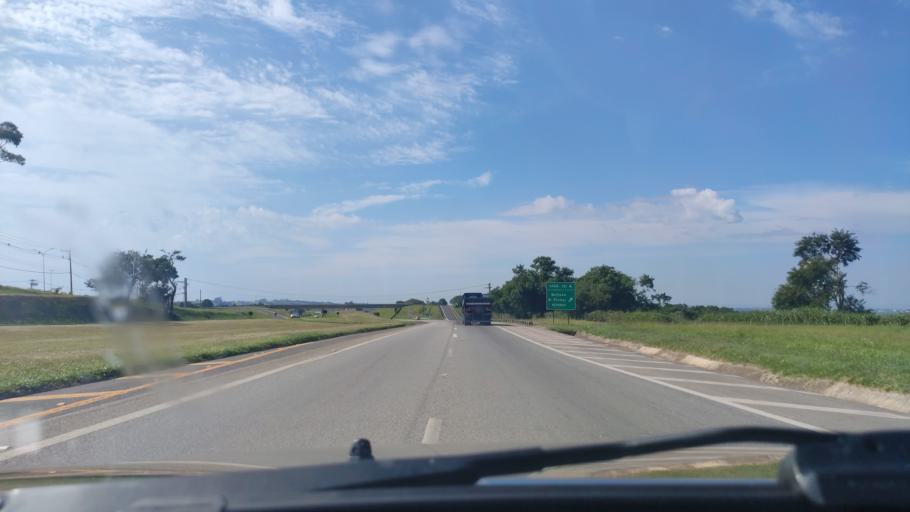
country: BR
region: Sao Paulo
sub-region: Boituva
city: Boituva
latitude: -23.3155
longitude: -47.6413
